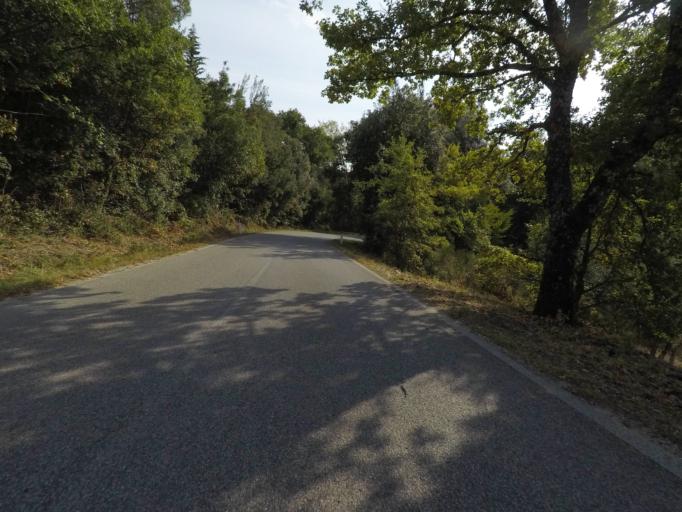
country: IT
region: Tuscany
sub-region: Provincia di Siena
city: Belverde
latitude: 43.4002
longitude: 11.3523
